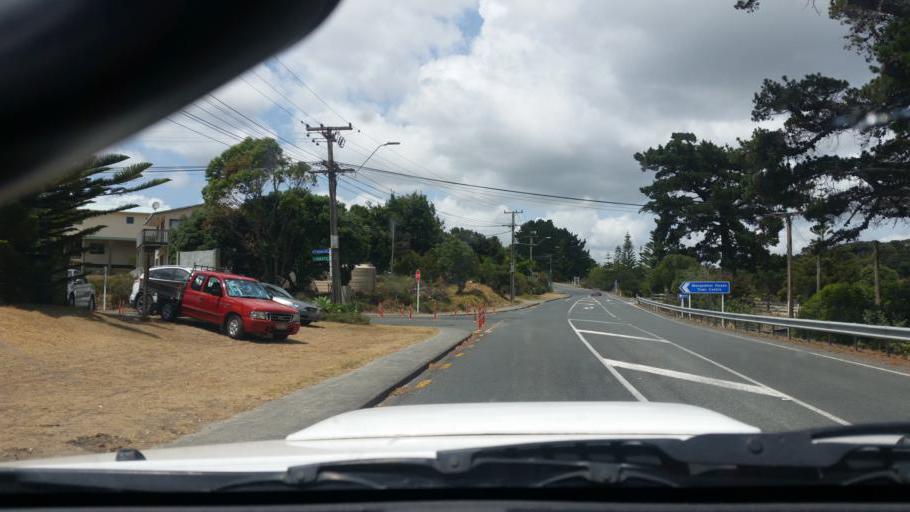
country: NZ
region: Auckland
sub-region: Auckland
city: Wellsford
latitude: -36.0951
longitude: 174.5860
